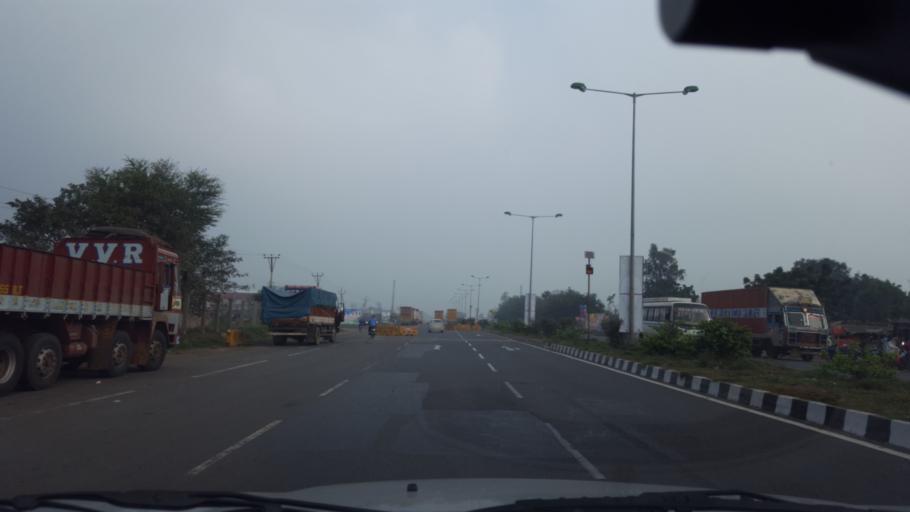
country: IN
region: Andhra Pradesh
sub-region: Prakasam
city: Addanki
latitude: 15.6849
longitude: 80.0180
